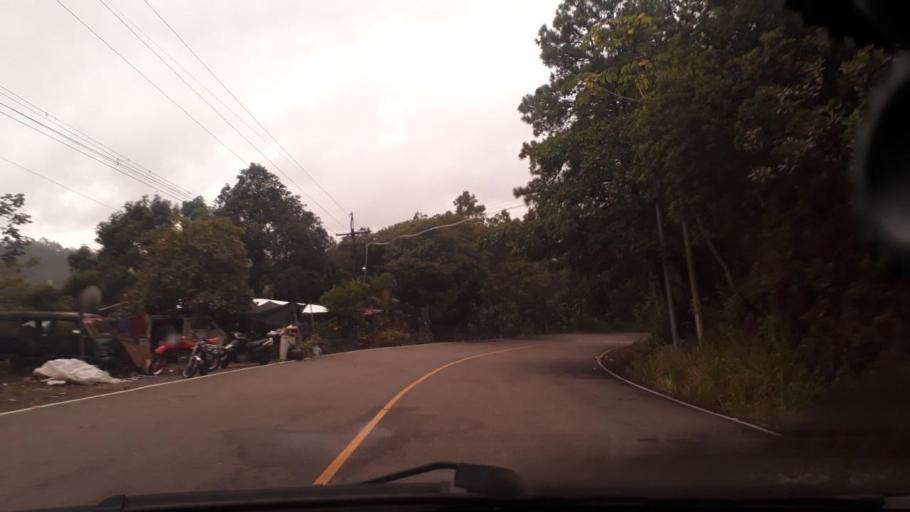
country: GT
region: Chiquimula
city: Esquipulas
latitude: 14.5387
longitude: -89.2836
